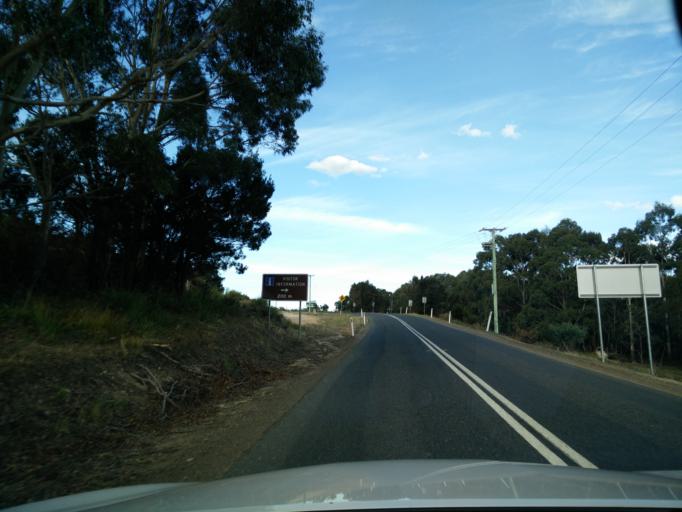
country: AU
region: Tasmania
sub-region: Break O'Day
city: St Helens
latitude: -41.9420
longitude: 148.2185
